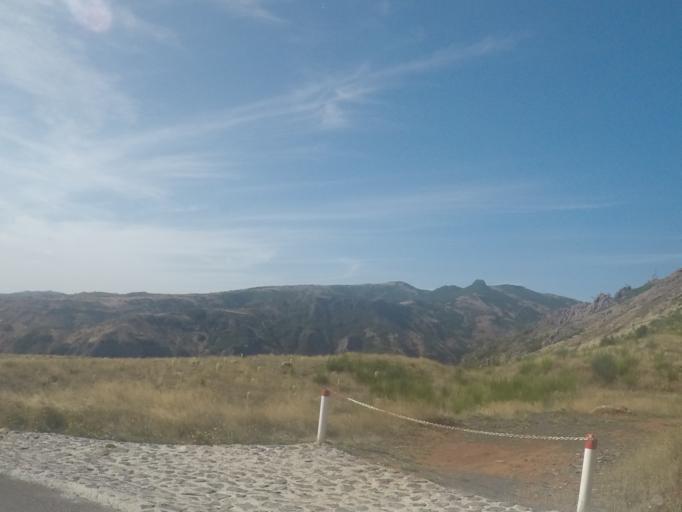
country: PT
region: Madeira
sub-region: Funchal
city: Nossa Senhora do Monte
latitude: 32.7089
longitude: -16.9142
